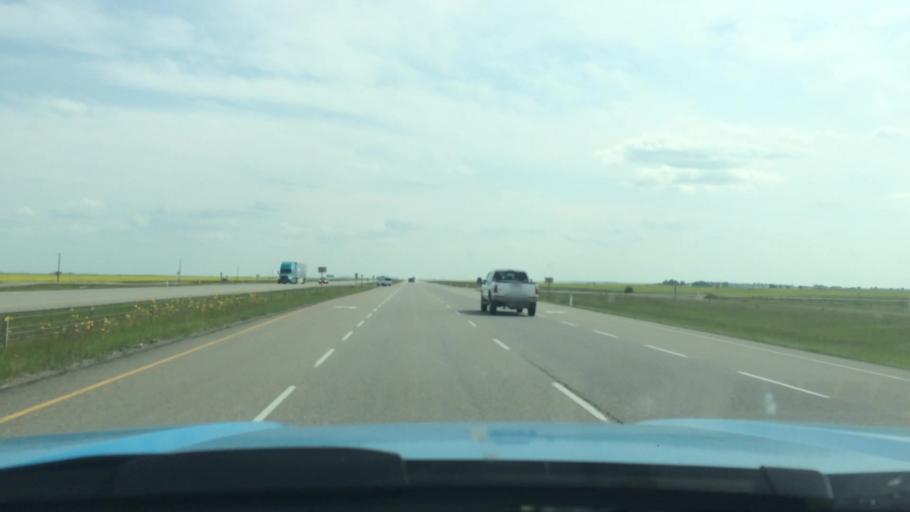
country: CA
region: Alberta
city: Carstairs
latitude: 51.6219
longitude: -114.0256
